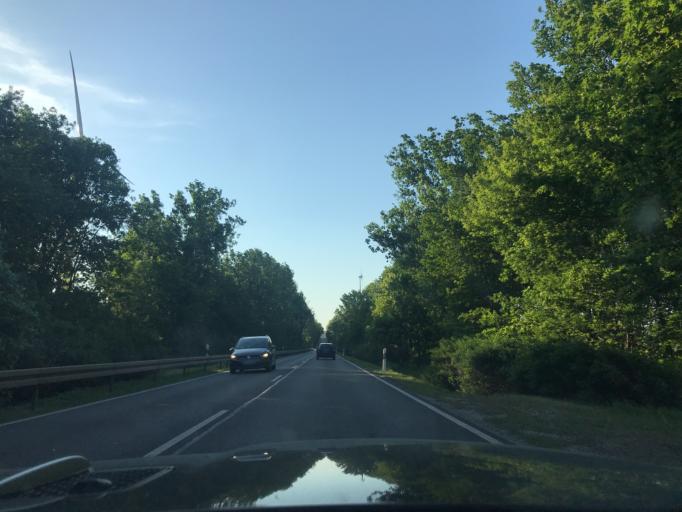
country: DE
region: Thuringia
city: Westhausen
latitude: 51.0262
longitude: 10.6770
